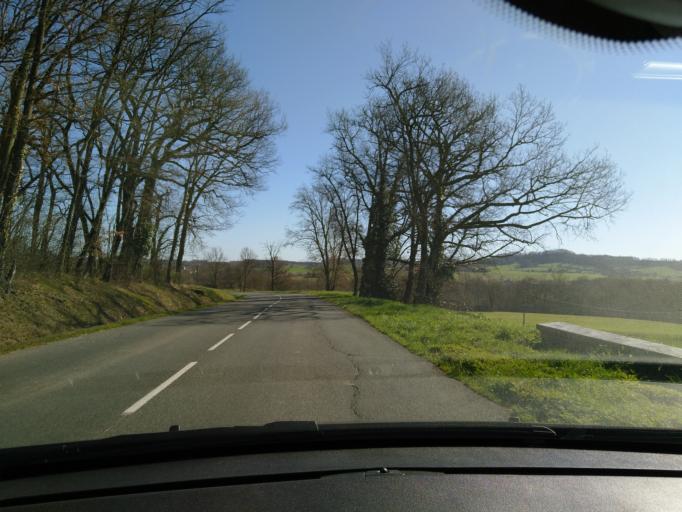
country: FR
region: Aquitaine
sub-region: Departement du Lot-et-Garonne
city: Cancon
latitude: 44.5337
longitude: 0.6528
